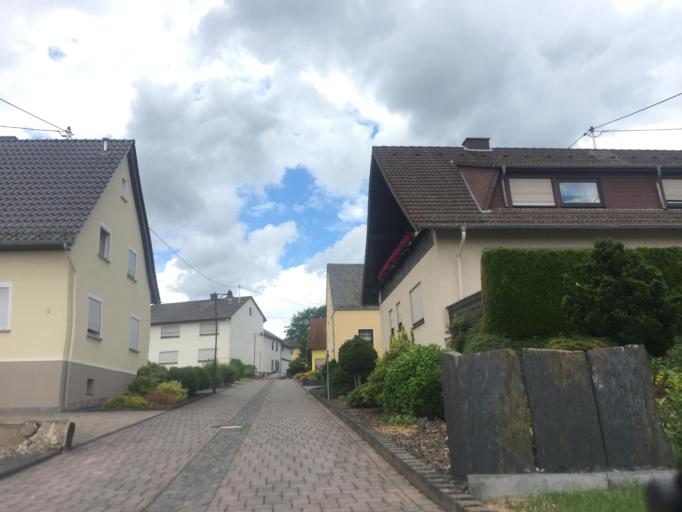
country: DE
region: Rheinland-Pfalz
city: Girod
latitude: 50.4499
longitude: 7.9085
